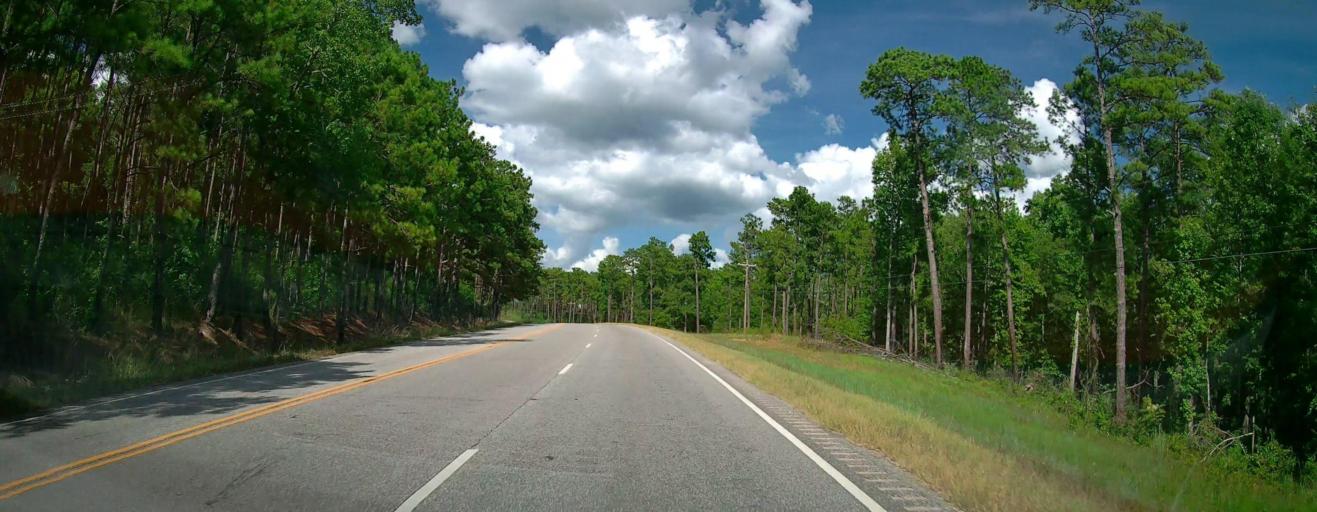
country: US
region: Alabama
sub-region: Macon County
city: Tuskegee
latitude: 32.4481
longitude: -85.6356
